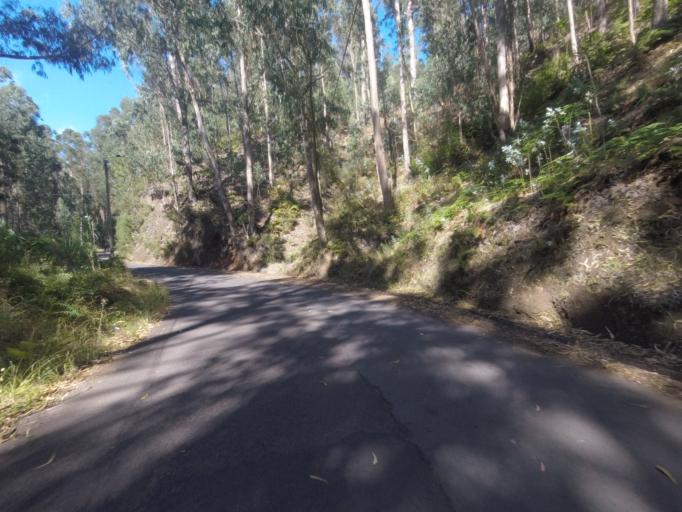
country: PT
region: Madeira
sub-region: Ribeira Brava
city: Campanario
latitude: 32.6886
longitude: -17.0209
